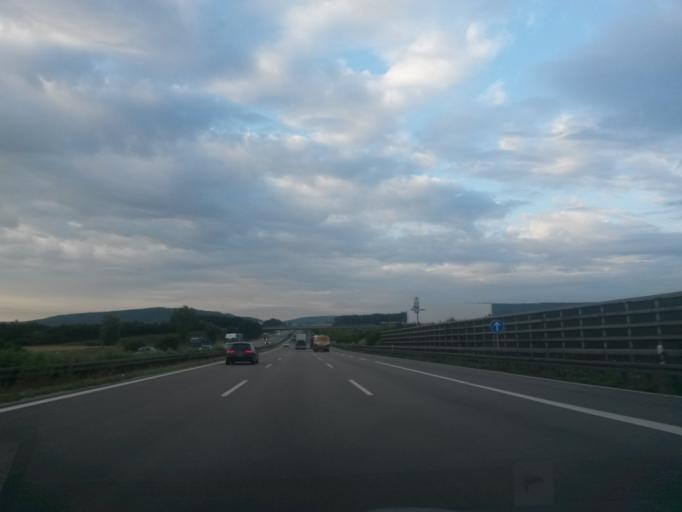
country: DE
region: Bavaria
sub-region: Upper Palatinate
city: Freystadt
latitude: 49.1660
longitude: 11.2629
